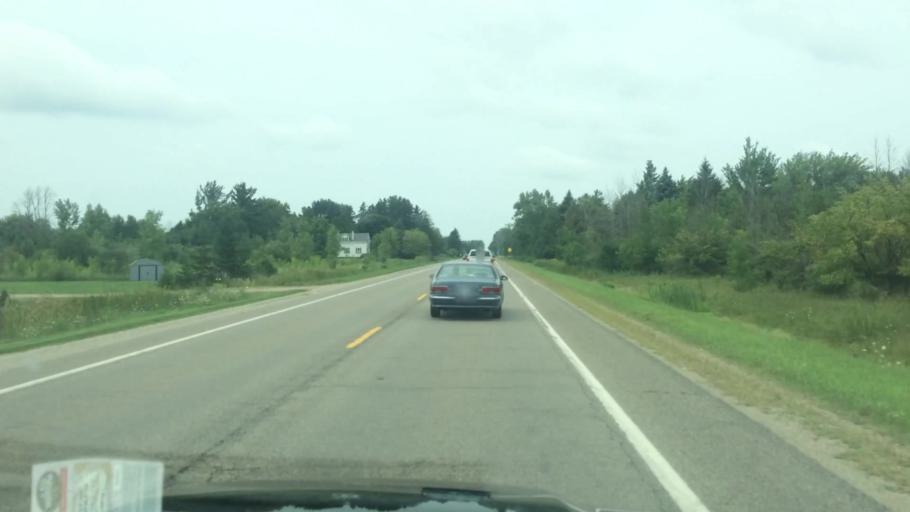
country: US
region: Michigan
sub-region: Huron County
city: Bad Axe
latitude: 43.8845
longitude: -83.0030
